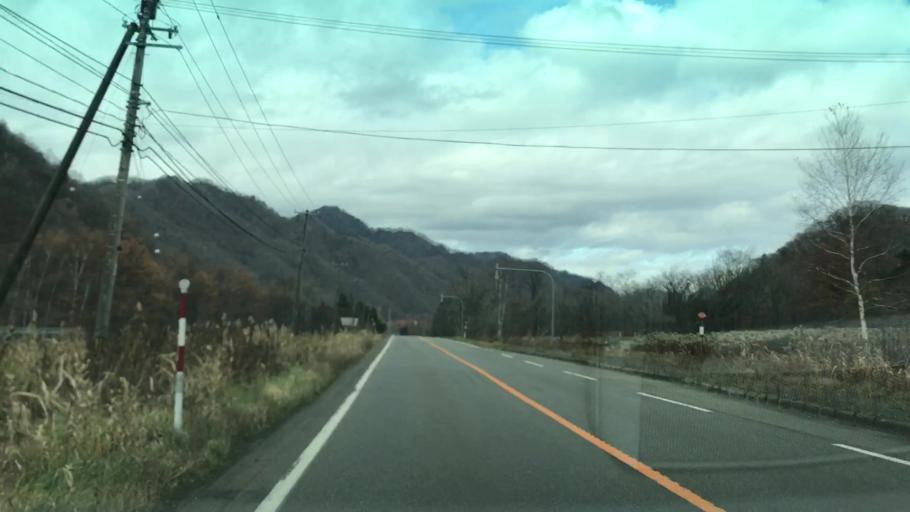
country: JP
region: Hokkaido
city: Shizunai-furukawacho
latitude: 42.8171
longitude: 142.4213
